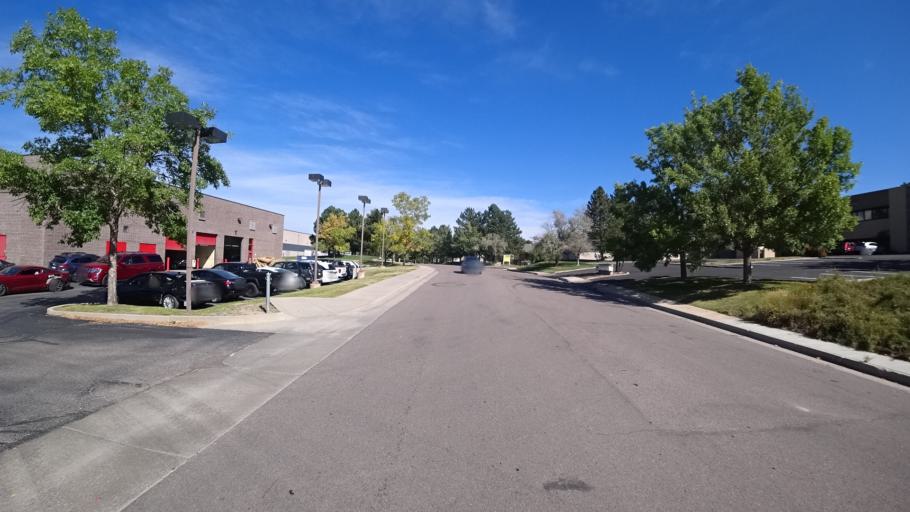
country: US
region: Colorado
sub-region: El Paso County
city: Colorado Springs
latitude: 38.9109
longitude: -104.7852
